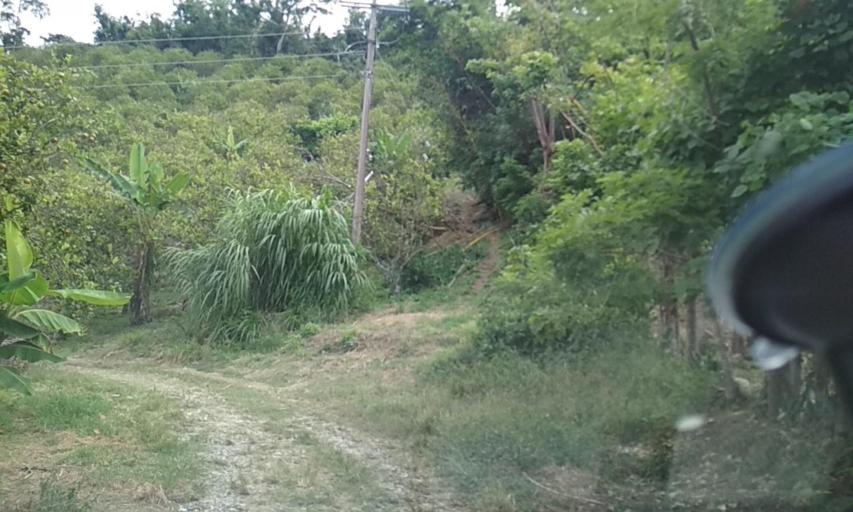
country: MX
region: Veracruz
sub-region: Papantla
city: Residencial Tajin
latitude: 20.6159
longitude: -97.3502
